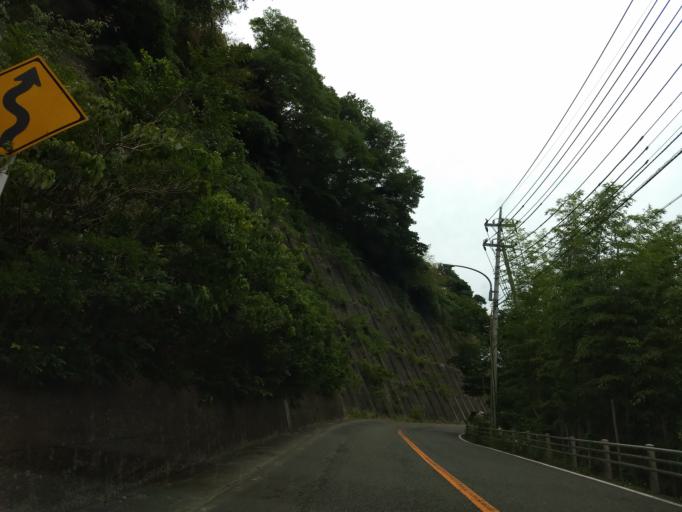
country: JP
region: Yamanashi
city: Uenohara
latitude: 35.6127
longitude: 139.0658
